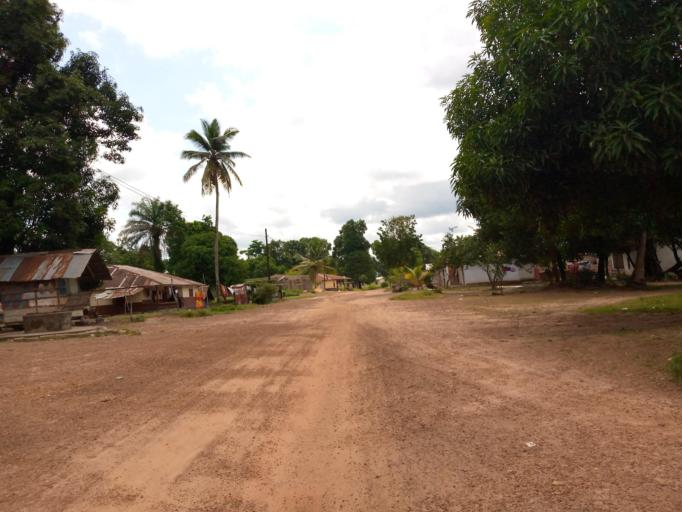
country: SL
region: Northern Province
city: Magburaka
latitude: 8.7120
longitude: -11.9348
